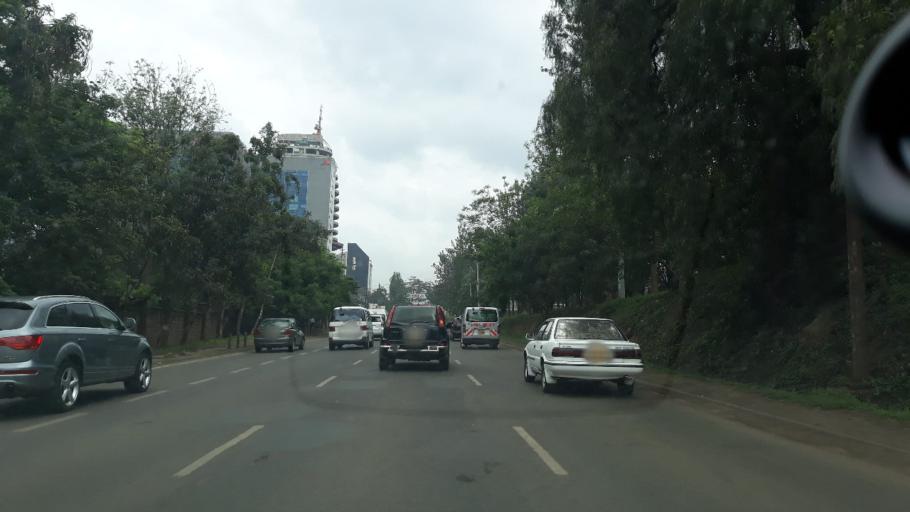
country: KE
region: Nairobi Area
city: Nairobi
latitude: -1.2673
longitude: 36.8042
